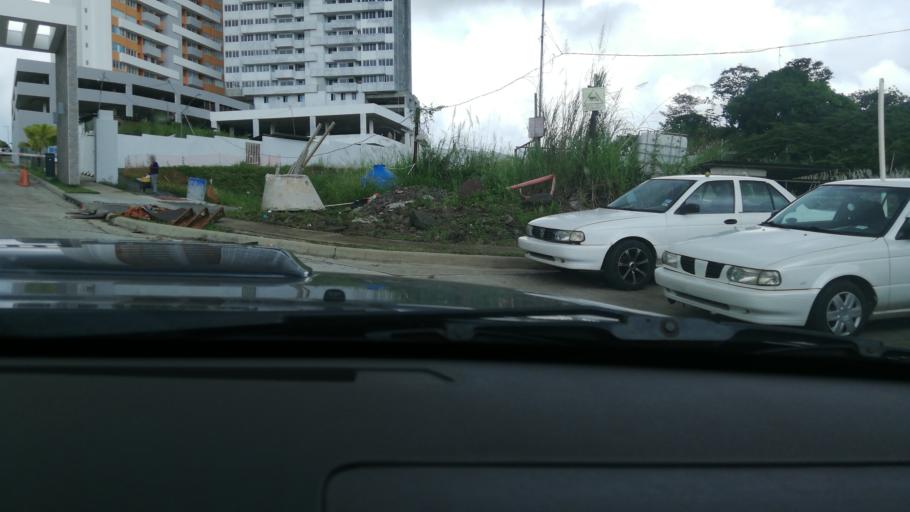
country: PA
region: Panama
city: San Miguelito
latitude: 9.0522
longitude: -79.4781
